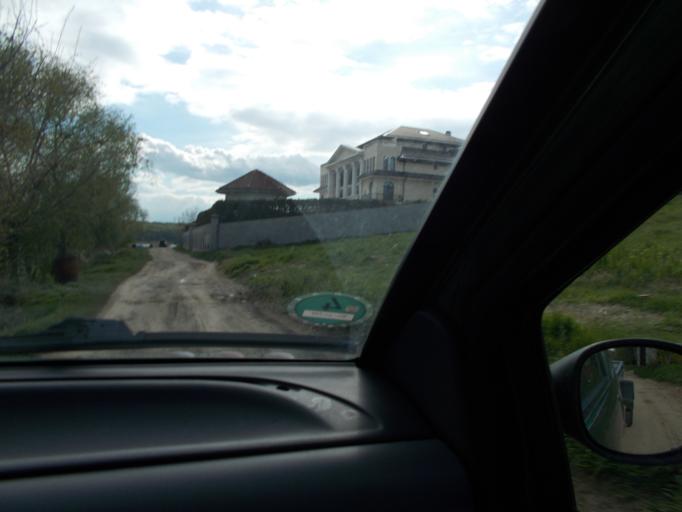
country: RO
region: Ilfov
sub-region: Comuna Branesti
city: Branesti
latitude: 44.4512
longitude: 26.3288
